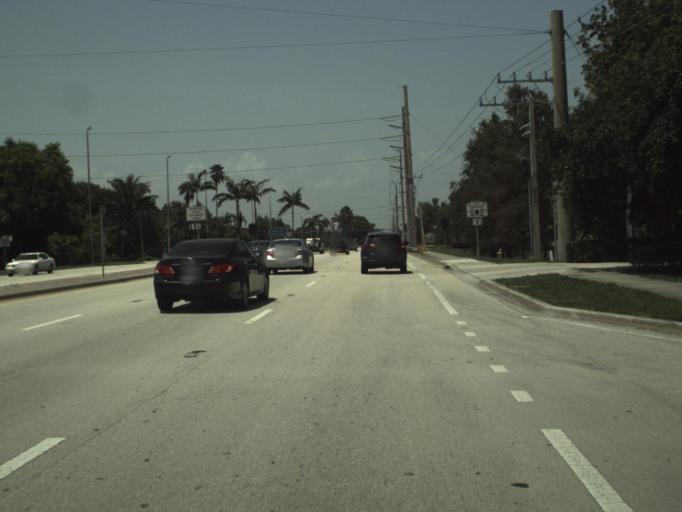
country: US
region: Florida
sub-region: Palm Beach County
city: Boca Pointe
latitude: 26.3053
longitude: -80.1524
